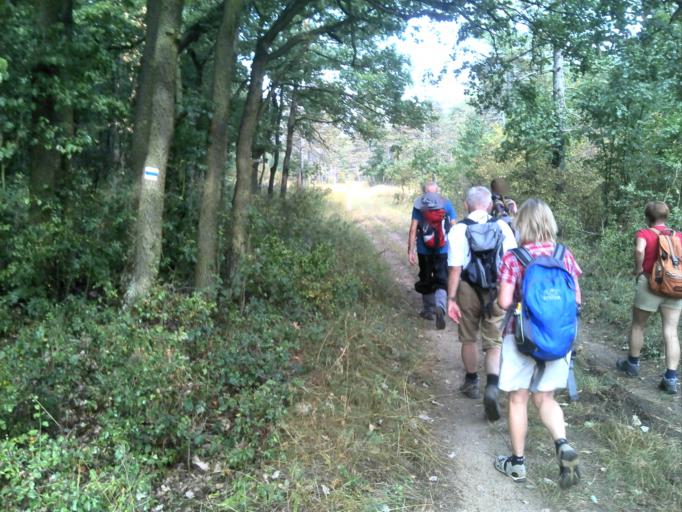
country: HU
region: Fejer
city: Csakvar
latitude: 47.4041
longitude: 18.3733
